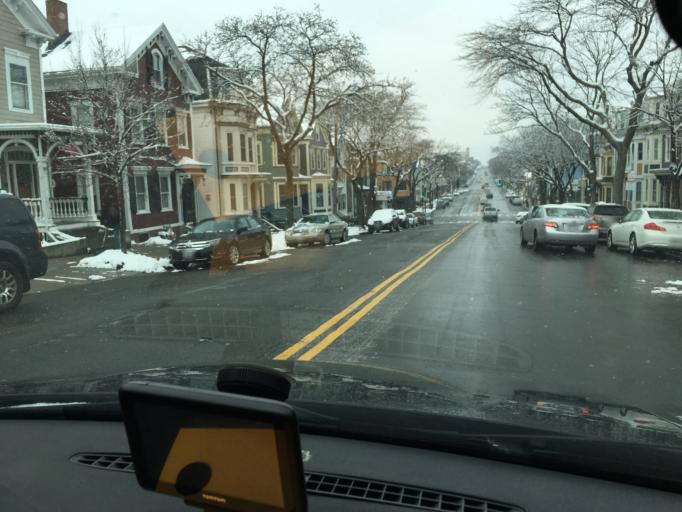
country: US
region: Massachusetts
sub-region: Suffolk County
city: South Boston
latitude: 42.3357
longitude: -71.0342
